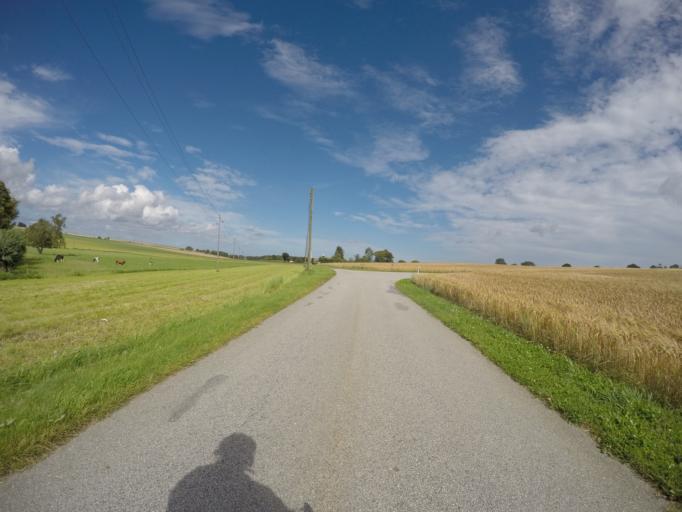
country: SE
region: Skane
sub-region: Simrishamns Kommun
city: Simrishamn
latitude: 55.4909
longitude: 14.2600
